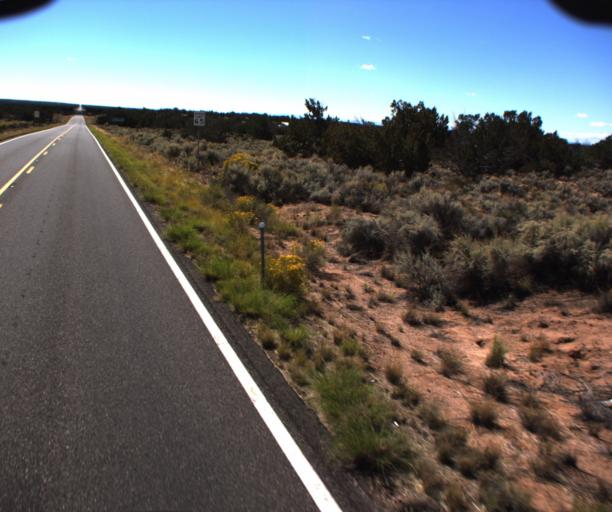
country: US
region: Arizona
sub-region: Apache County
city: Houck
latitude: 34.8961
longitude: -109.2381
